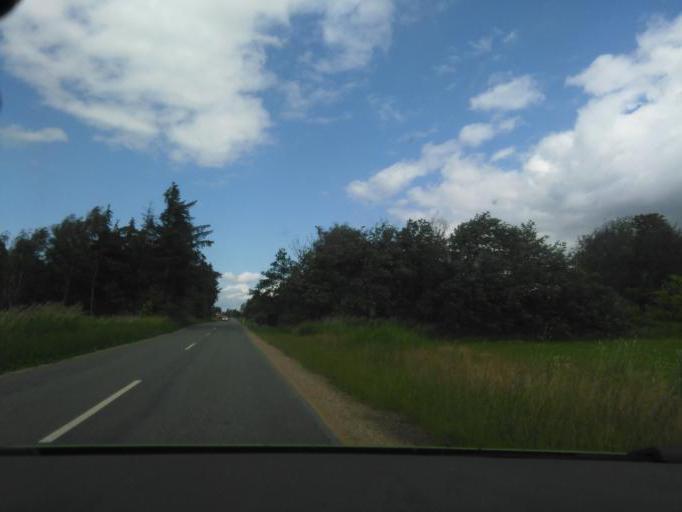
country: DK
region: Zealand
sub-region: Kalundborg Kommune
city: Gorlev
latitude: 55.5397
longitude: 11.1676
